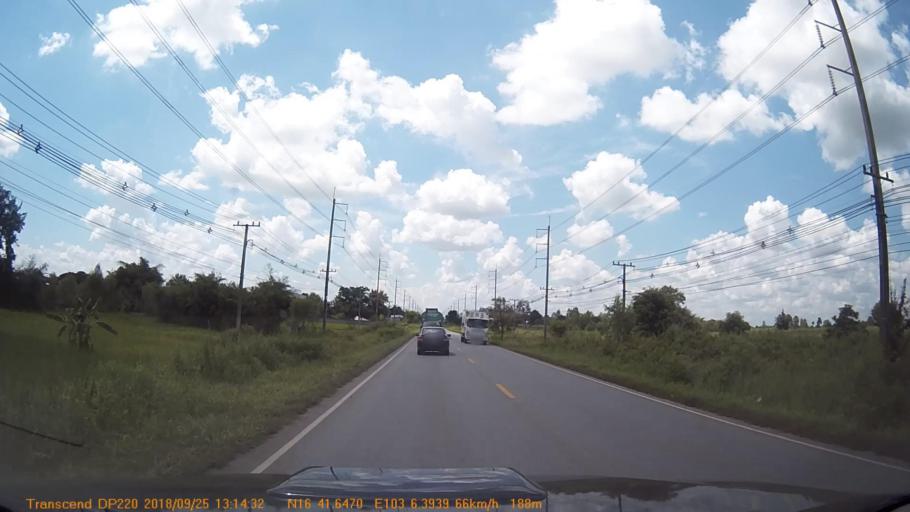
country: TH
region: Khon Kaen
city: Kranuan
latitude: 16.6941
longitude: 103.1067
